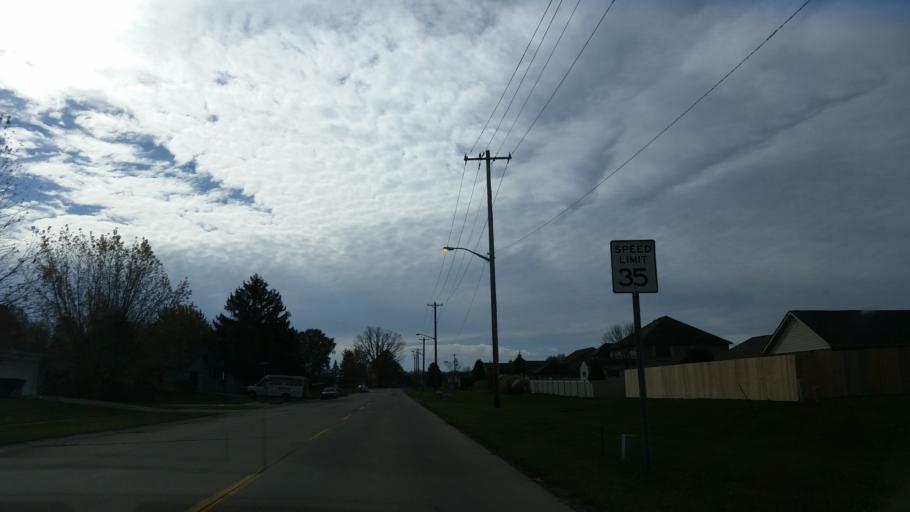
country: US
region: Indiana
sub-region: Howard County
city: Indian Heights
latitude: 40.4500
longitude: -86.1556
